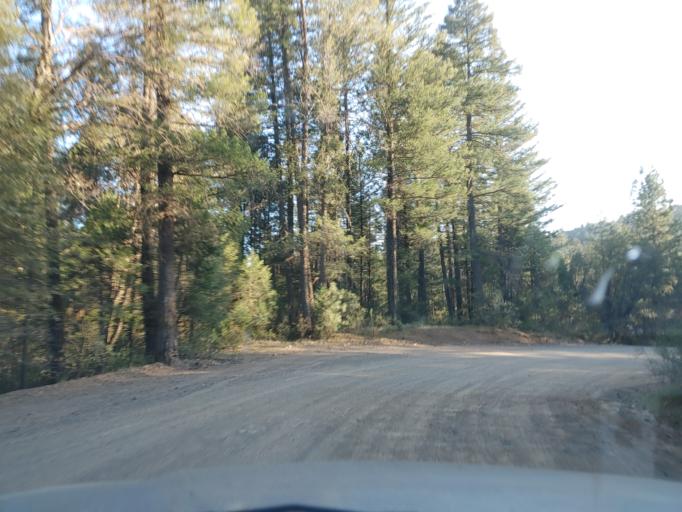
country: US
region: California
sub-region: Shasta County
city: Bella Vista
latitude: 40.8105
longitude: -121.9975
